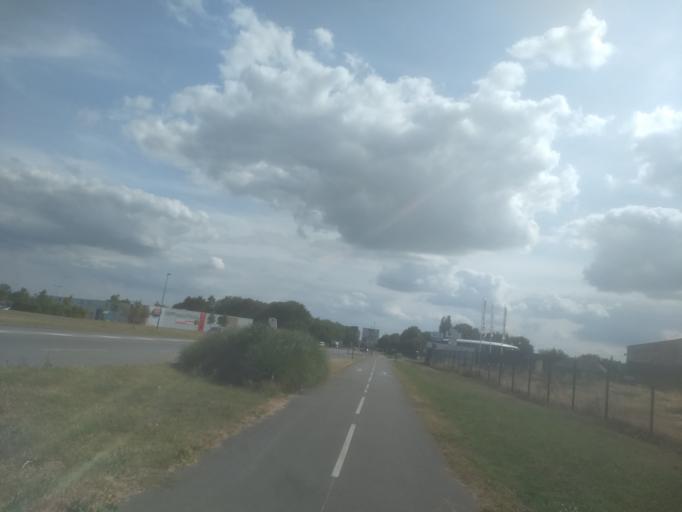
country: FR
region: Nord-Pas-de-Calais
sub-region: Departement du Pas-de-Calais
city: Beaurains
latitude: 50.2644
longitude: 2.7958
